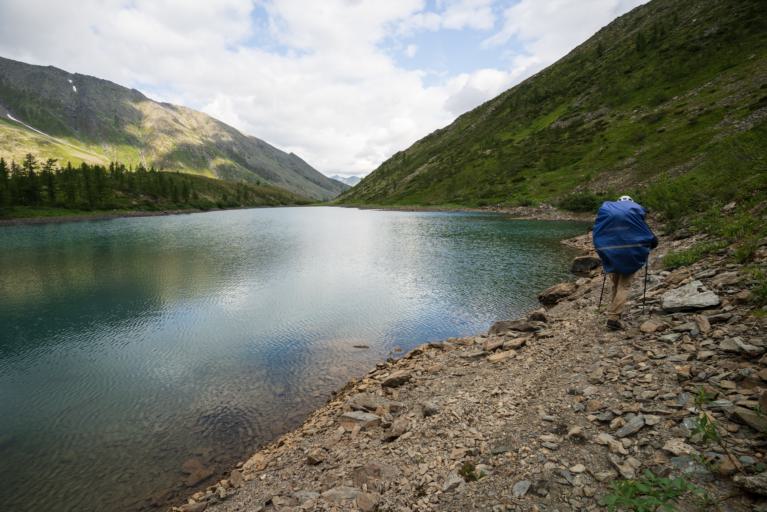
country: RU
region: Komi Republic
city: Synya
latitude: 64.8439
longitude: 59.3398
